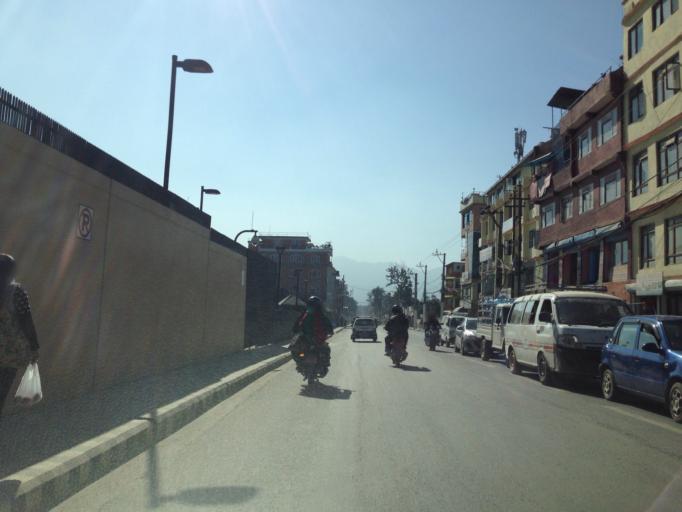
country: NP
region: Central Region
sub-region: Bagmati Zone
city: Kathmandu
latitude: 27.7388
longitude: 85.3359
